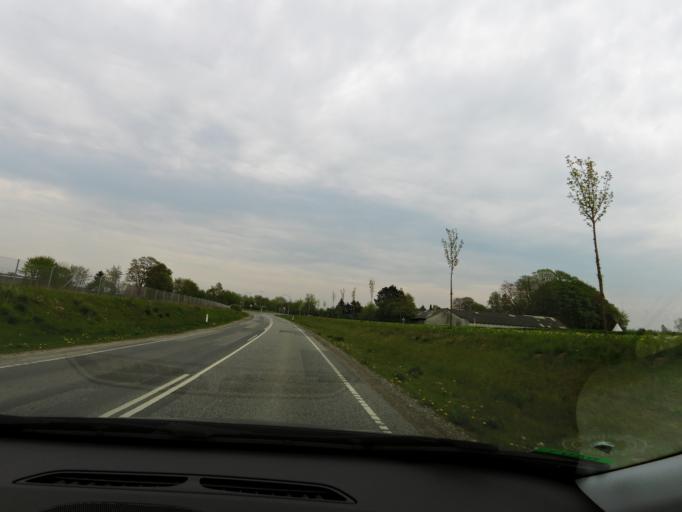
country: DK
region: South Denmark
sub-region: Faaborg-Midtfyn Kommune
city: Arslev
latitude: 55.3040
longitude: 10.4492
